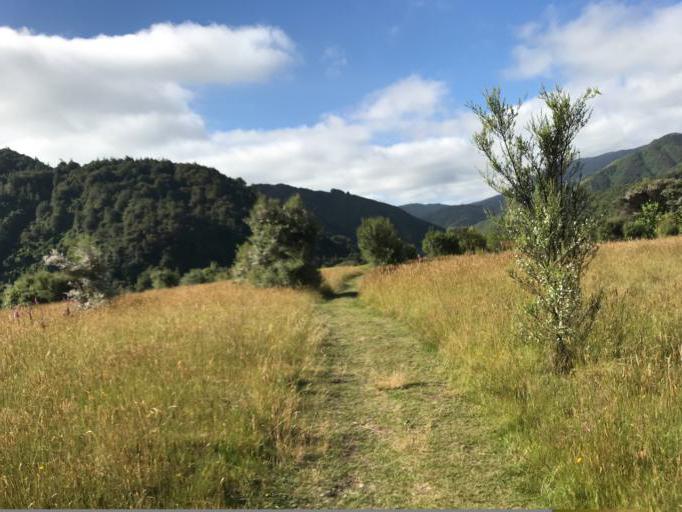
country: NZ
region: Wellington
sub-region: Kapiti Coast District
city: Otaki
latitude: -40.8732
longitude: 175.2345
